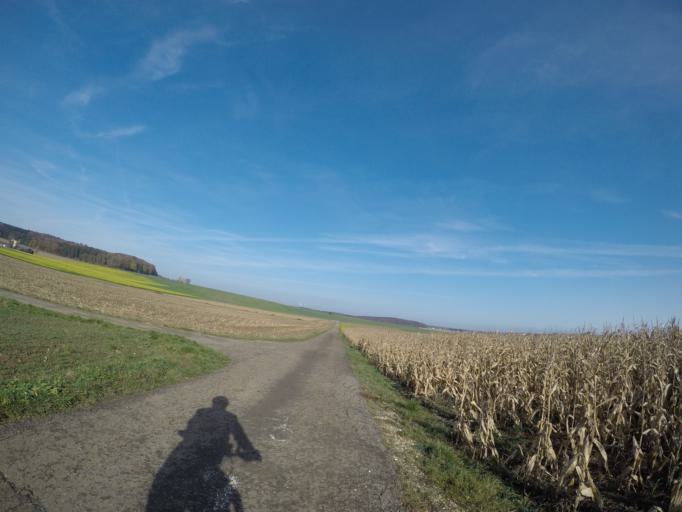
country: DE
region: Baden-Wuerttemberg
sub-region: Tuebingen Region
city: Bernstadt
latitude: 48.4875
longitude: 10.0067
